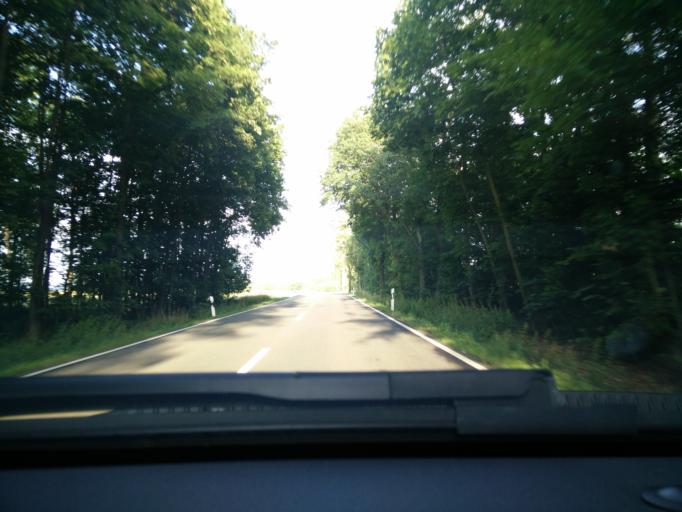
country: DE
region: Saxony
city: Konigsfeld
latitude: 51.0717
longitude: 12.7282
